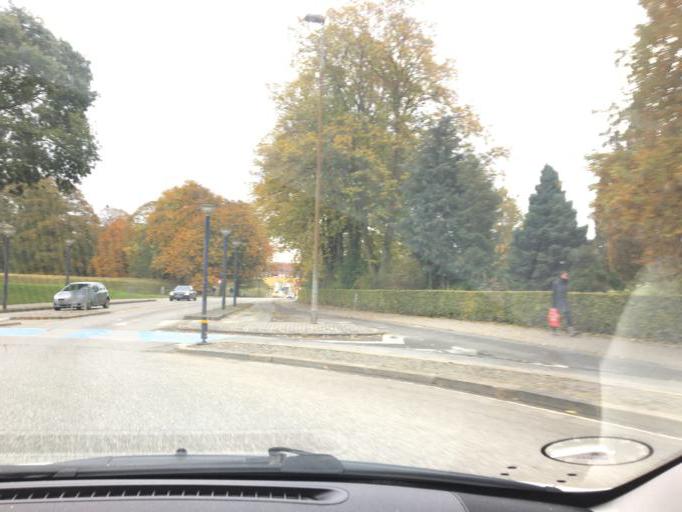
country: DK
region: South Denmark
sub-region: Fredericia Kommune
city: Fredericia
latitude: 55.5688
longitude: 9.7494
